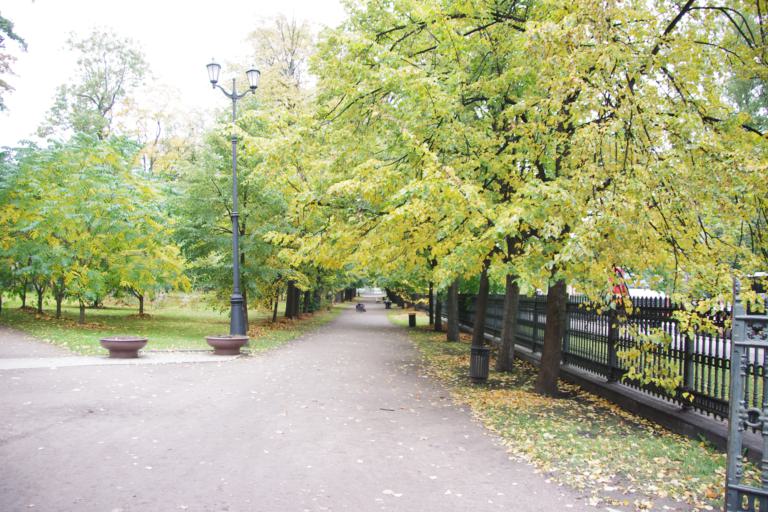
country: RU
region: St.-Petersburg
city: Kronshtadt
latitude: 59.9876
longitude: 29.7693
